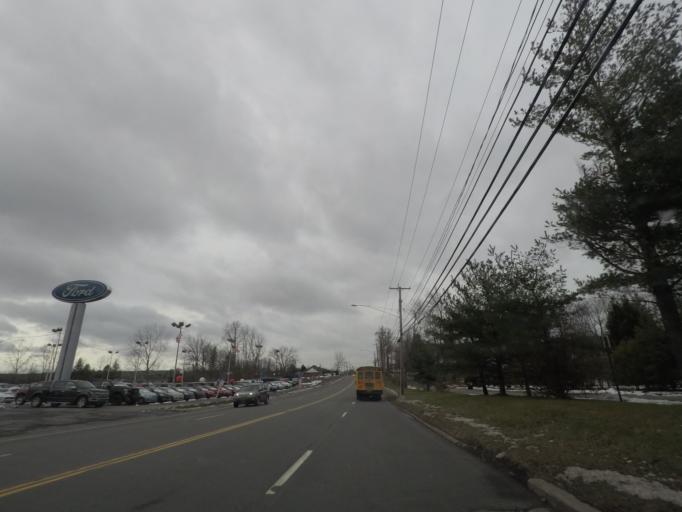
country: US
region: New York
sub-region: Rensselaer County
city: East Greenbush
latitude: 42.5940
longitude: -73.7050
